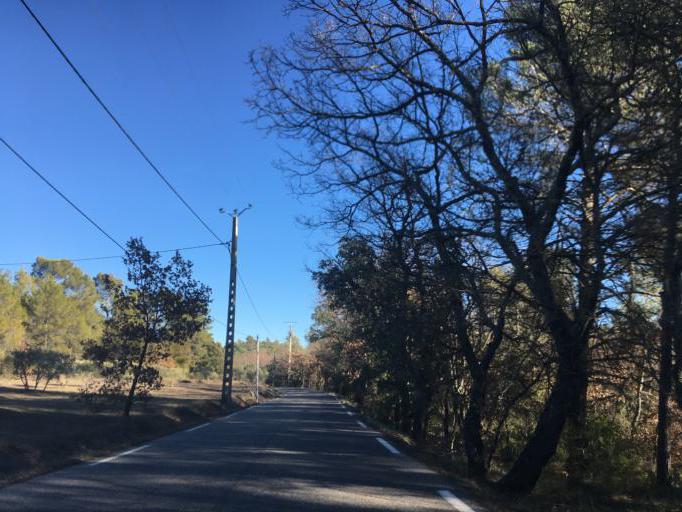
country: FR
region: Provence-Alpes-Cote d'Azur
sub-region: Departement du Var
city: Barjols
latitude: 43.5928
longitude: 6.0458
